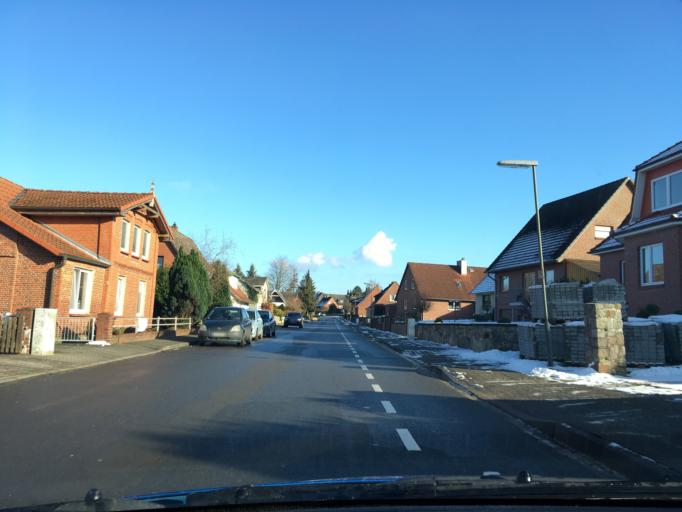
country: DE
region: Schleswig-Holstein
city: Gulzow
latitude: 53.4421
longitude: 10.4848
